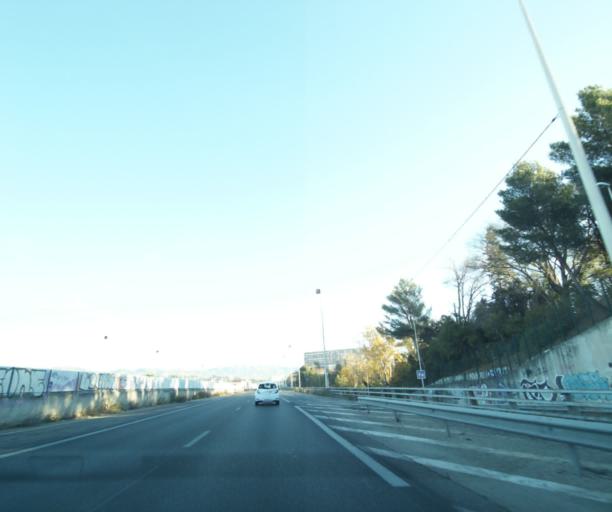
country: FR
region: Provence-Alpes-Cote d'Azur
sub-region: Departement des Bouches-du-Rhone
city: Marseille 13
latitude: 43.3190
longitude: 5.4145
